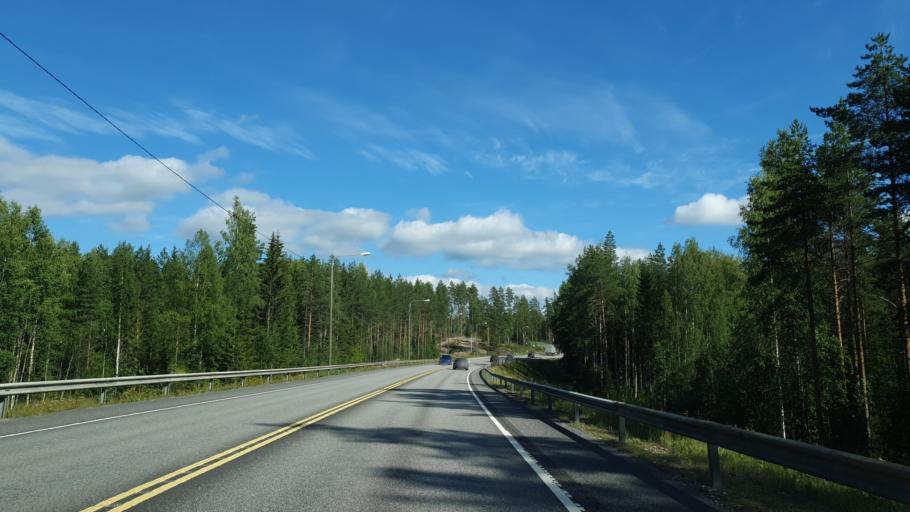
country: FI
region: Central Finland
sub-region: Jyvaeskylae
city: Toivakka
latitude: 62.2511
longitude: 26.1190
